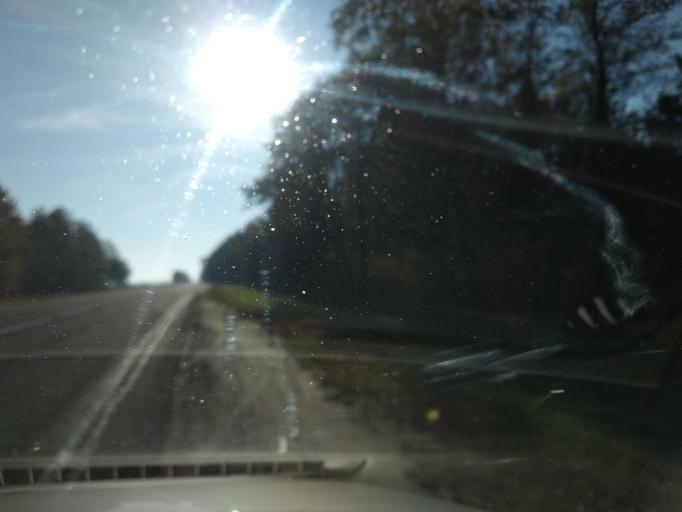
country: BY
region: Brest
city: Malaryta
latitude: 51.8733
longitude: 24.1772
